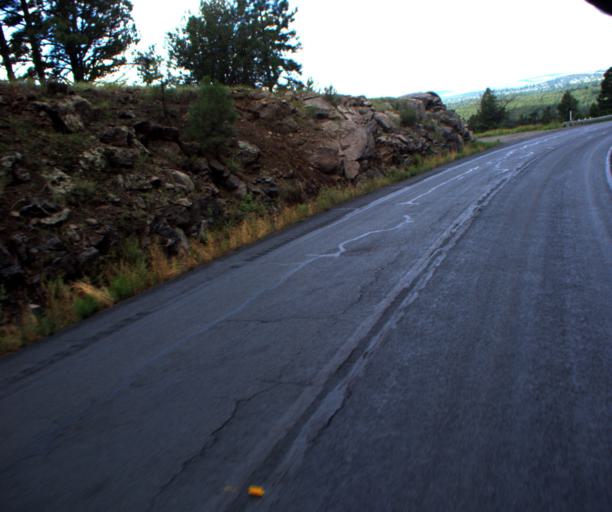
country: US
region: Arizona
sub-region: Gila County
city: Pine
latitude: 34.5148
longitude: -111.4938
